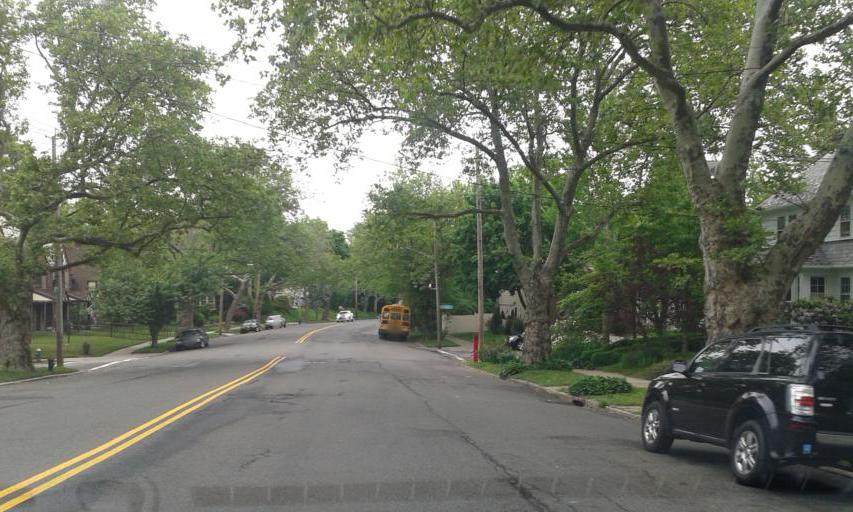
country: US
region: New Jersey
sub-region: Hudson County
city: Bayonne
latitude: 40.6319
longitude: -74.1006
